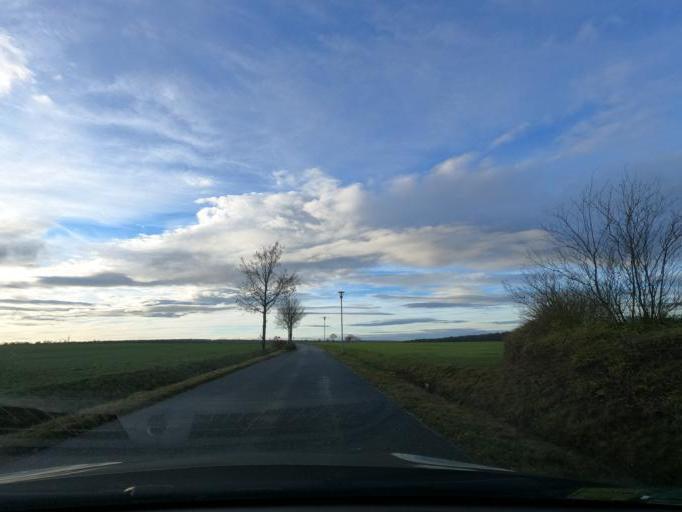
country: DE
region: Lower Saxony
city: Wolfenbuettel
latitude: 52.1498
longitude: 10.5214
